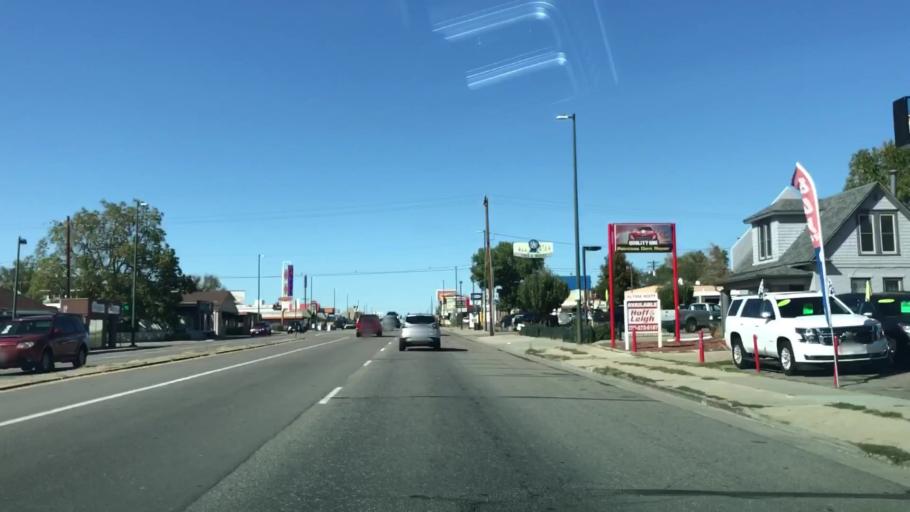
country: US
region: Colorado
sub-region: Arapahoe County
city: Englewood
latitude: 39.6343
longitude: -104.9878
